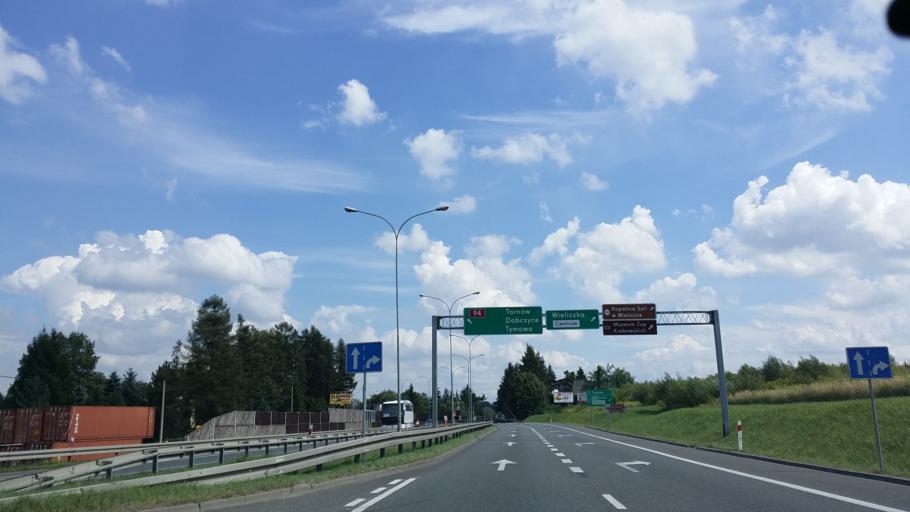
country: PL
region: Lesser Poland Voivodeship
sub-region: Powiat wielicki
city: Wieliczka
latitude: 49.9951
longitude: 20.0373
